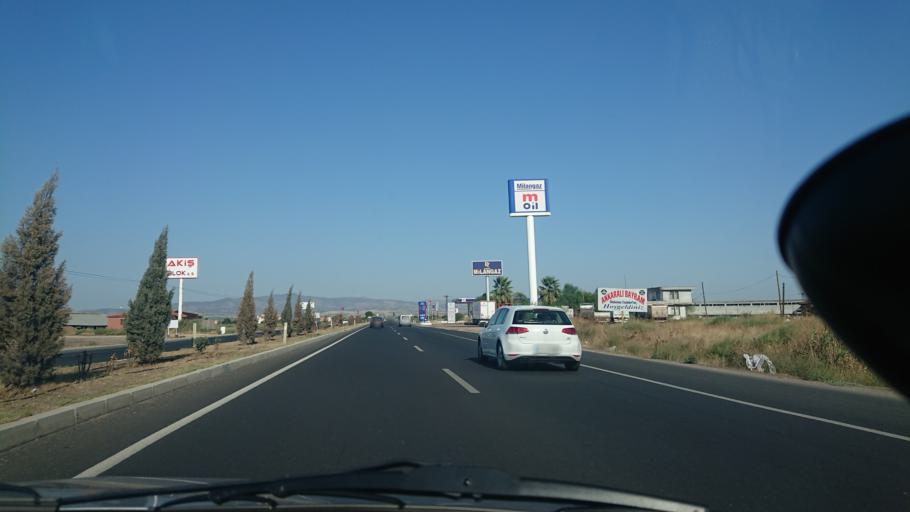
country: TR
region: Manisa
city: Salihli
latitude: 38.5049
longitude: 28.2251
